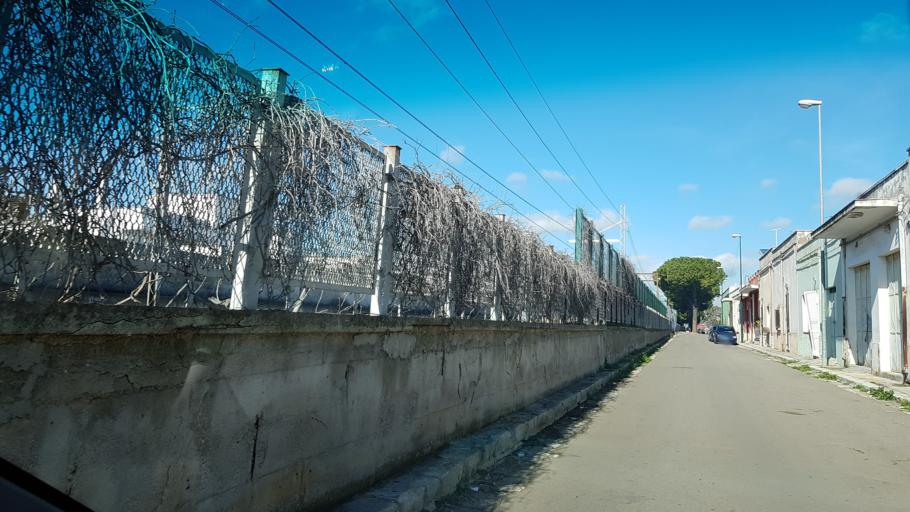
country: IT
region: Apulia
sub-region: Provincia di Lecce
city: Squinzano
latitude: 40.4330
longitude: 18.0528
